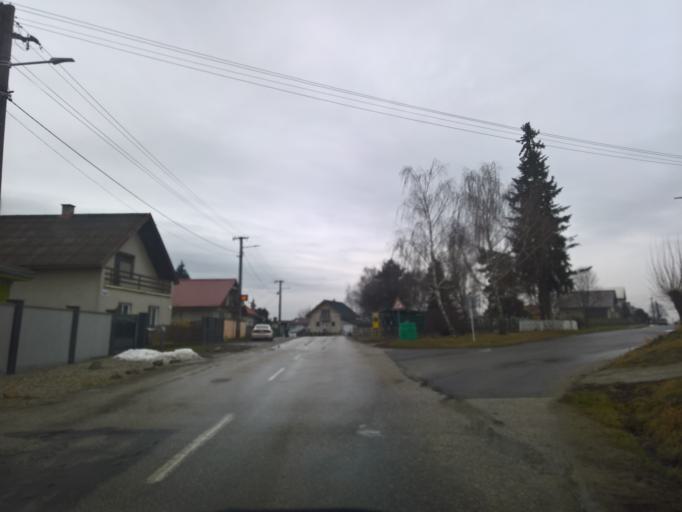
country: SK
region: Nitriansky
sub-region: Okres Nitra
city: Nitra
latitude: 48.2781
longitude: 17.9612
